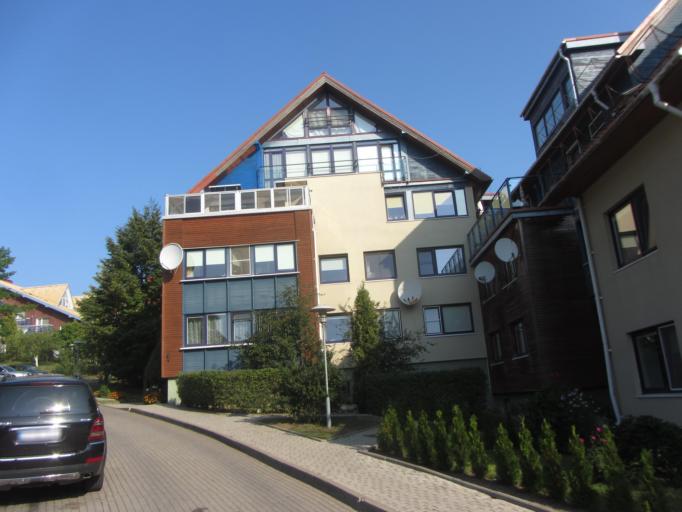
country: LT
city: Nida
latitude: 55.3031
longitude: 21.0011
